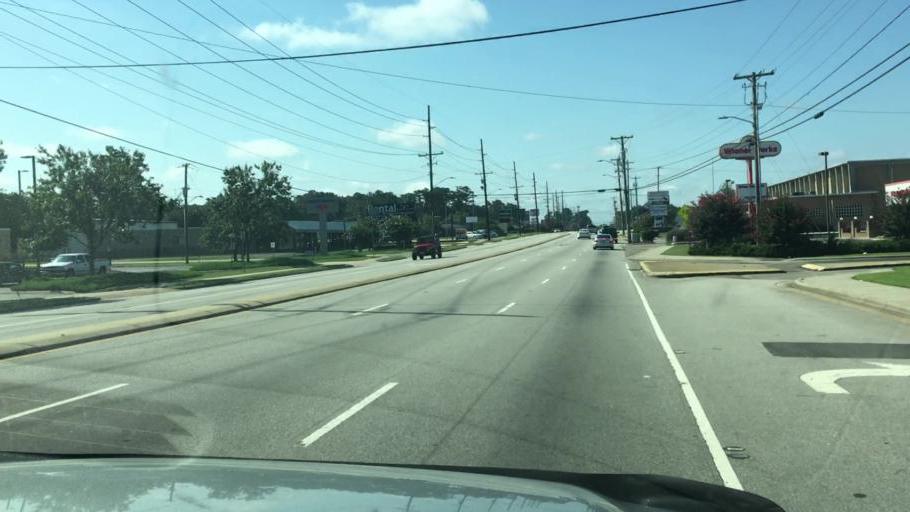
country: US
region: North Carolina
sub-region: Cumberland County
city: Fayetteville
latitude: 35.1117
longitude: -78.8795
